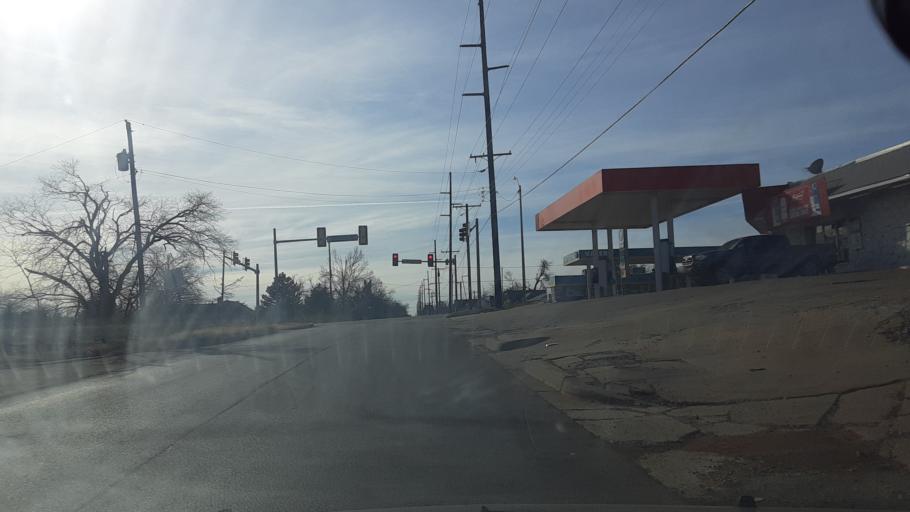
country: US
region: Oklahoma
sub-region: Logan County
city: Guthrie
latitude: 35.8807
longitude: -97.4075
